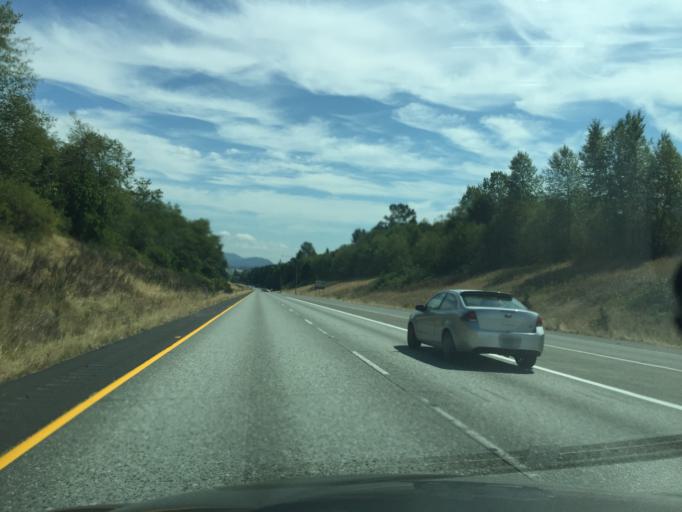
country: US
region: Washington
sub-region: Skagit County
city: Burlington
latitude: 48.5347
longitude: -122.3535
